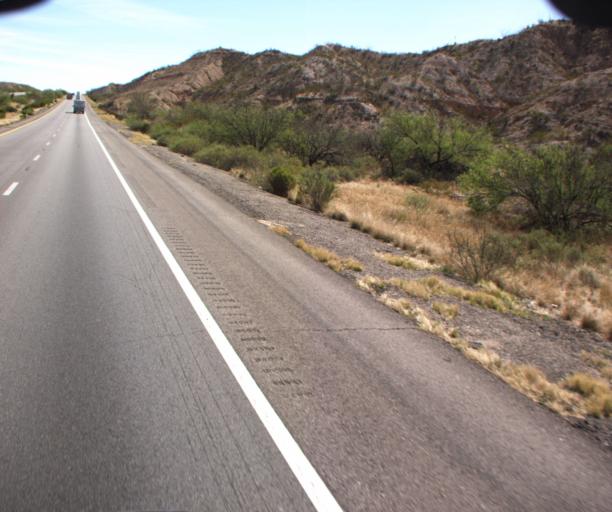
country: US
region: Arizona
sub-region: Cochise County
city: Saint David
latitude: 31.9805
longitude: -110.2159
